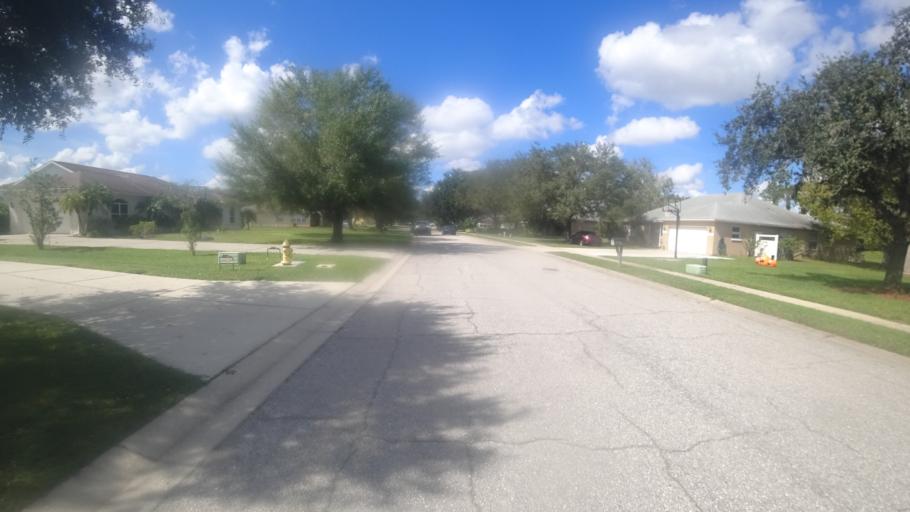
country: US
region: Florida
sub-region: Manatee County
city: Ellenton
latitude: 27.5021
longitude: -82.4050
